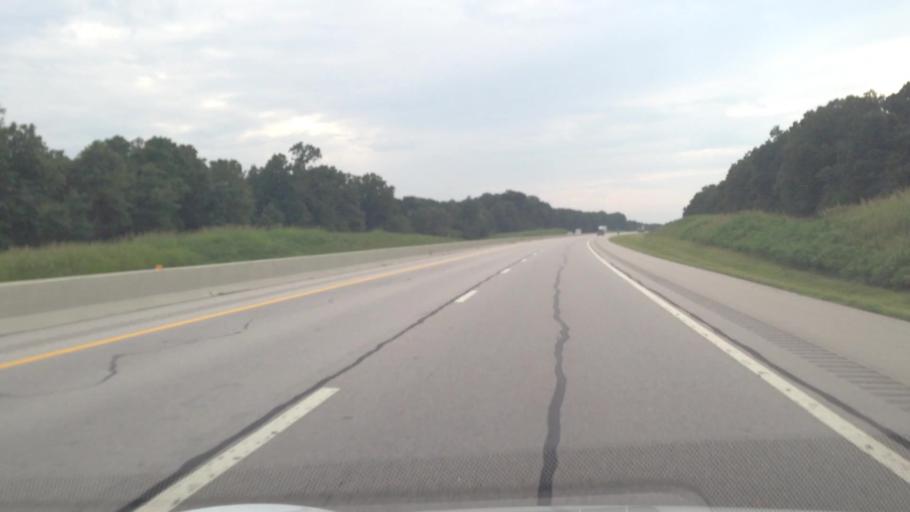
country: US
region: Kansas
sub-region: Cherokee County
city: Baxter Springs
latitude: 36.9414
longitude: -94.6893
